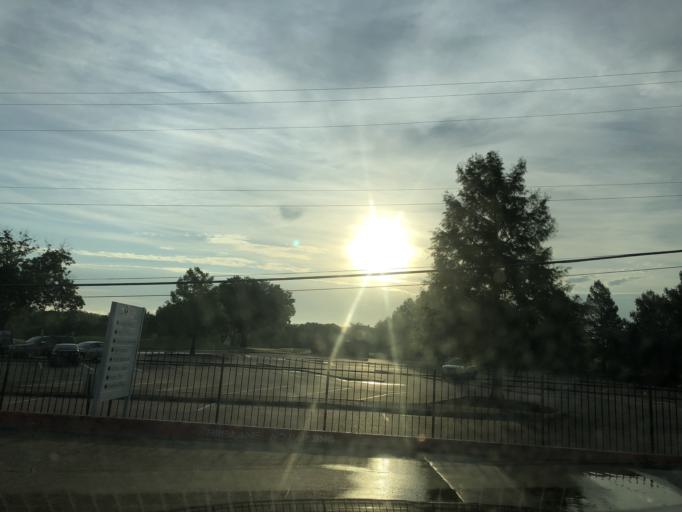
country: US
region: Texas
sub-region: Dallas County
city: Sunnyvale
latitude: 32.8355
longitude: -96.6113
